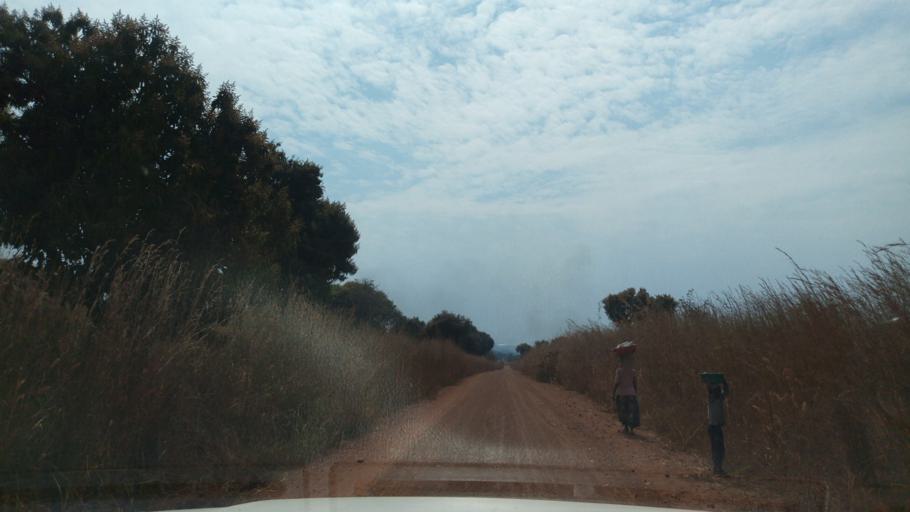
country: ZM
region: Northern
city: Kaputa
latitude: -8.4033
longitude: 28.9392
